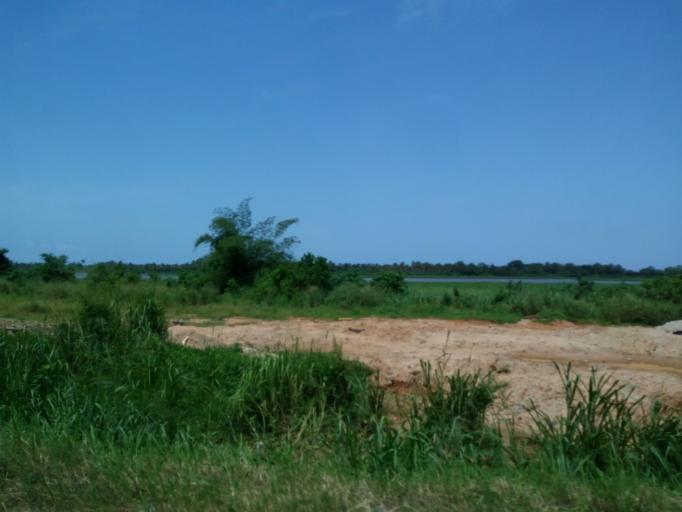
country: CI
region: Sud-Comoe
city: Grand-Bassam
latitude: 5.2185
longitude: -3.7192
